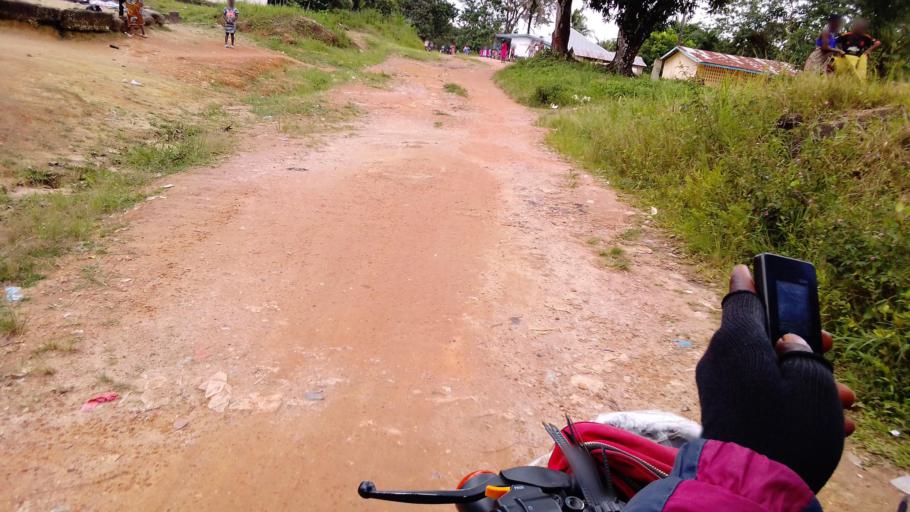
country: SL
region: Eastern Province
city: Koidu
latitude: 8.6749
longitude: -10.9802
